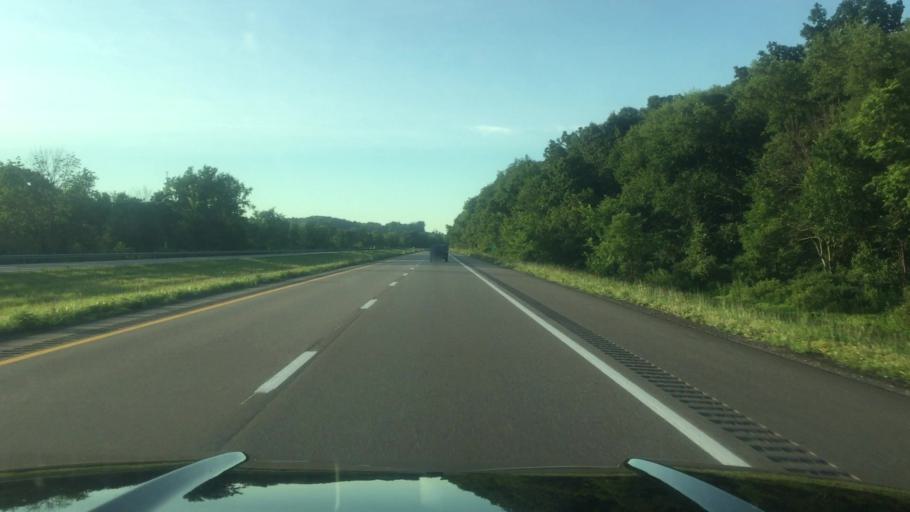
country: US
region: Ohio
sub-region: Tuscarawas County
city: Newcomerstown
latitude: 40.3282
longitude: -81.5693
